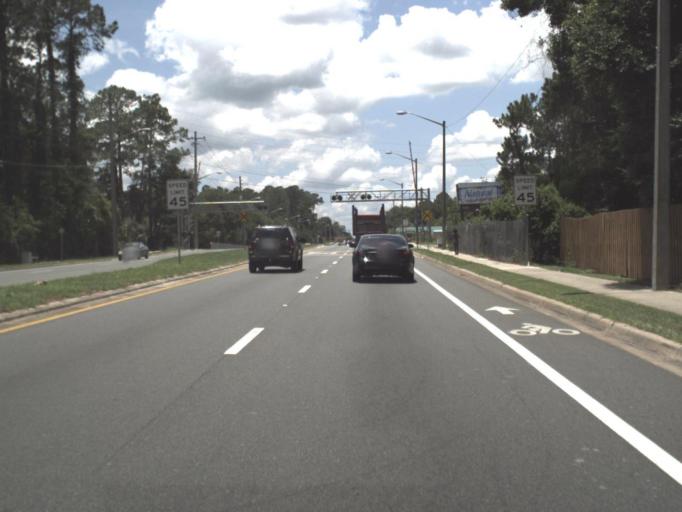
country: US
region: Florida
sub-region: Alachua County
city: Gainesville
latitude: 29.6885
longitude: -82.3245
